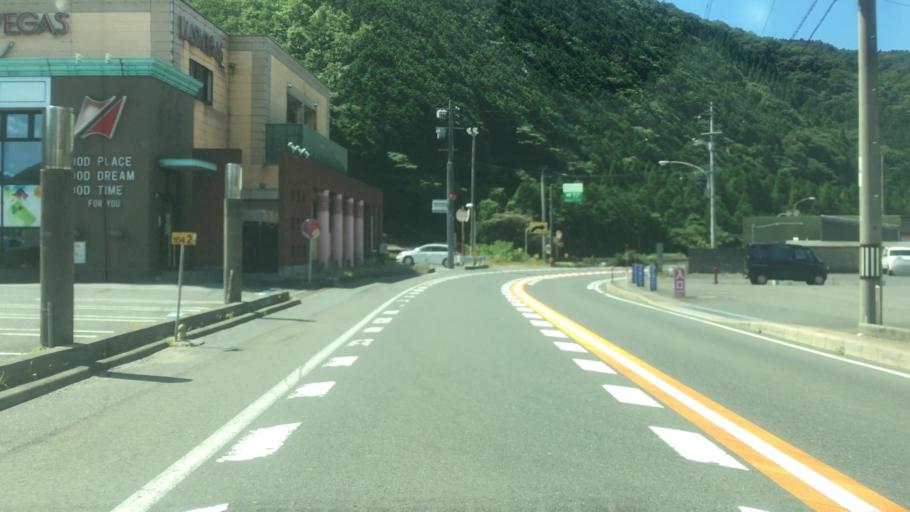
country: JP
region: Tottori
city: Tottori
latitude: 35.2722
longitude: 134.2246
